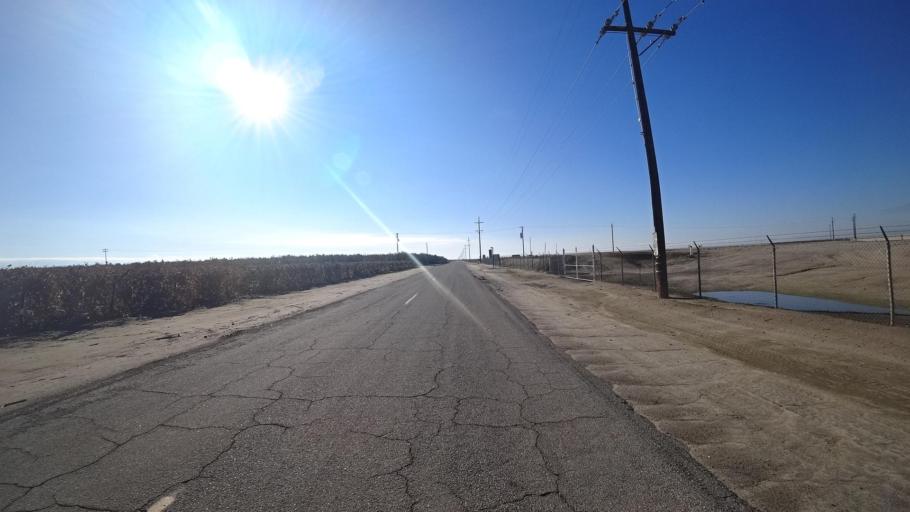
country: US
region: California
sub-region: Kern County
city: McFarland
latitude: 35.6828
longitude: -119.2766
